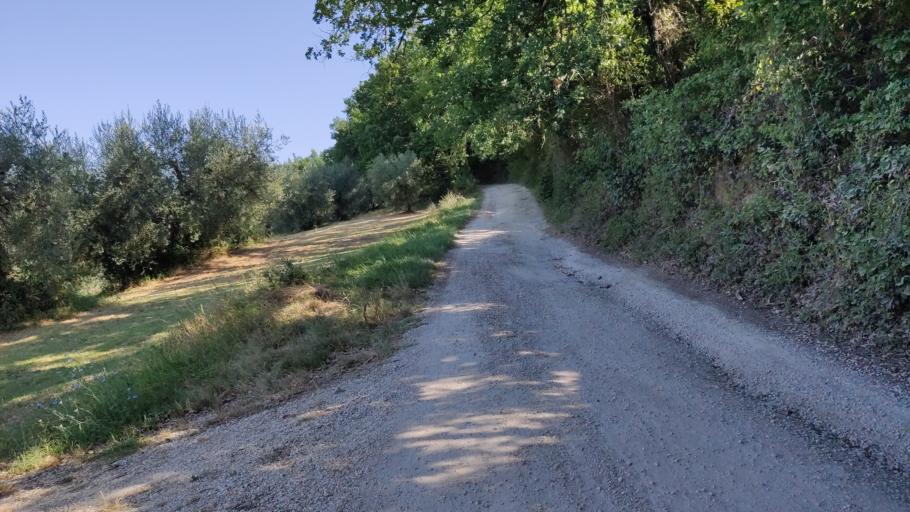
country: IT
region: Umbria
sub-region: Provincia di Terni
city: Amelia
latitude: 42.5299
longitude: 12.4102
